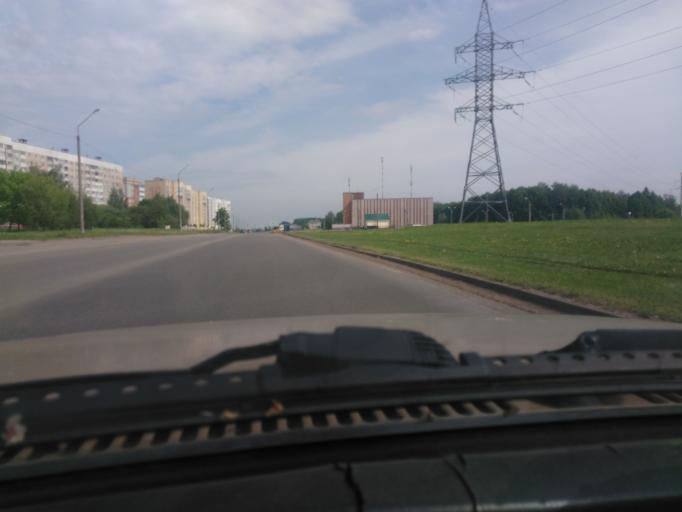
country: BY
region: Mogilev
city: Mahilyow
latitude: 53.9460
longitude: 30.3597
